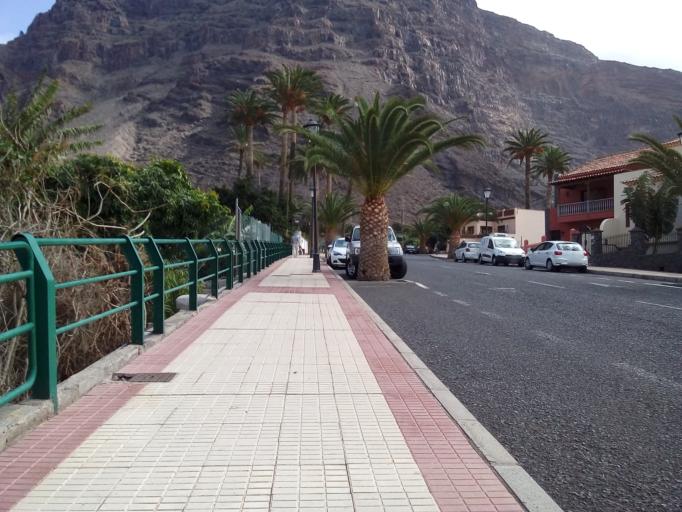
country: ES
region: Canary Islands
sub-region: Provincia de Santa Cruz de Tenerife
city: Alajero
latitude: 28.0948
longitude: -17.3379
